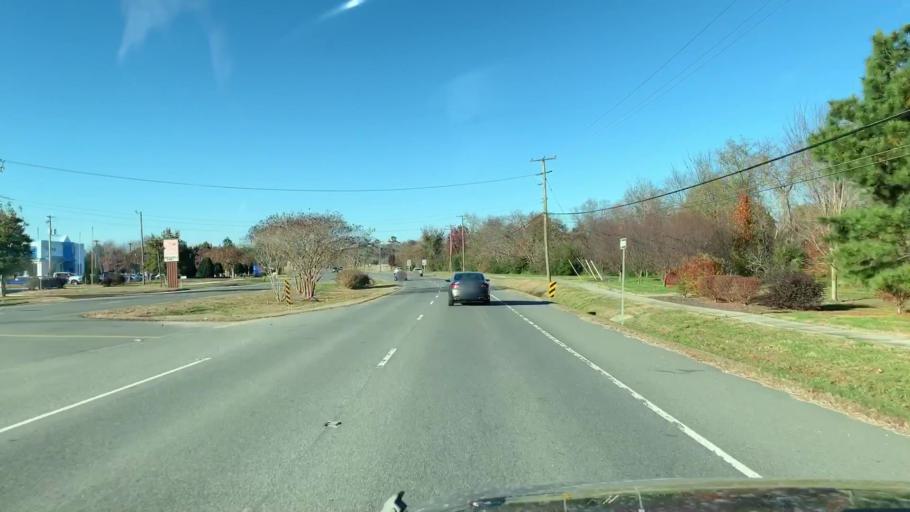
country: US
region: Virginia
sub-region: James City County
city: Williamsburg
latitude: 37.3573
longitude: -76.7642
